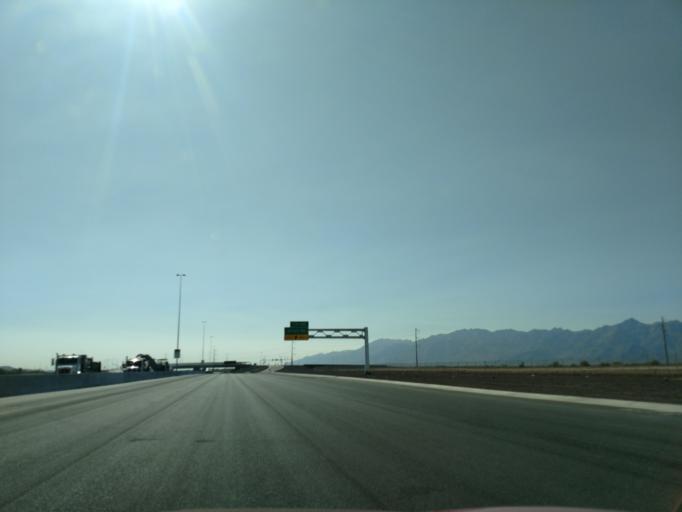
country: US
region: Arizona
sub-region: Maricopa County
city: Laveen
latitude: 33.3539
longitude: -112.1917
